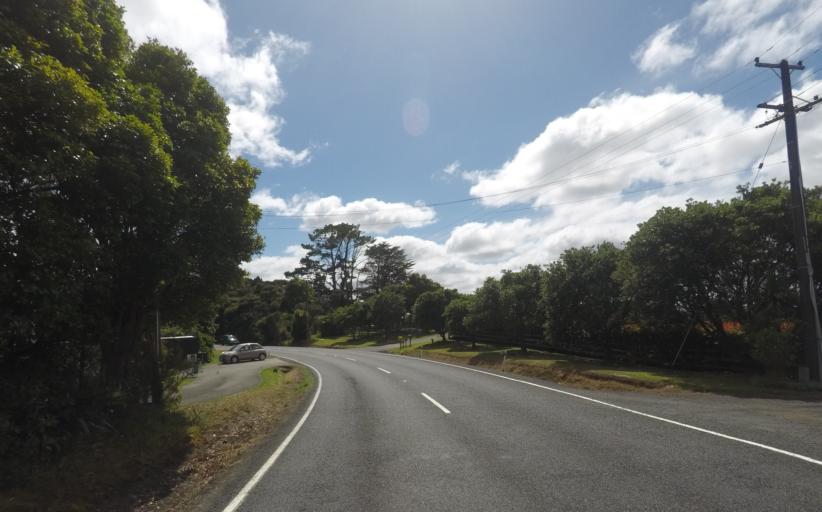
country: NZ
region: Auckland
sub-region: Auckland
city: Muriwai Beach
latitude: -36.8556
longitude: 174.5266
